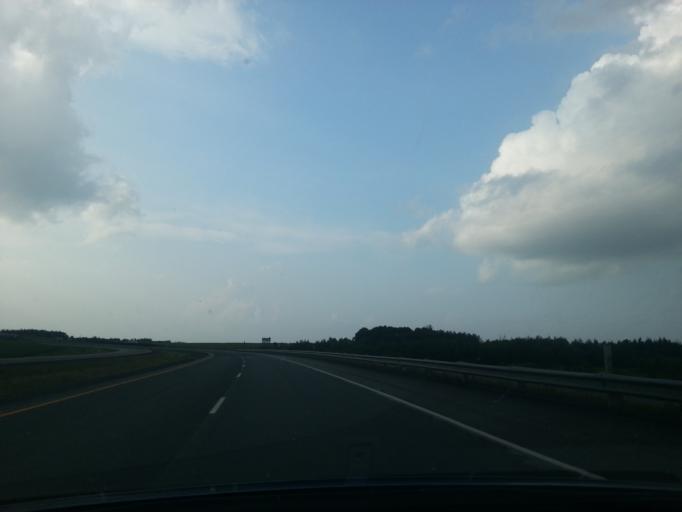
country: CA
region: New Brunswick
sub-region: Madawaska County
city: Saint-Leonard
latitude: 47.0876
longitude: -67.7771
